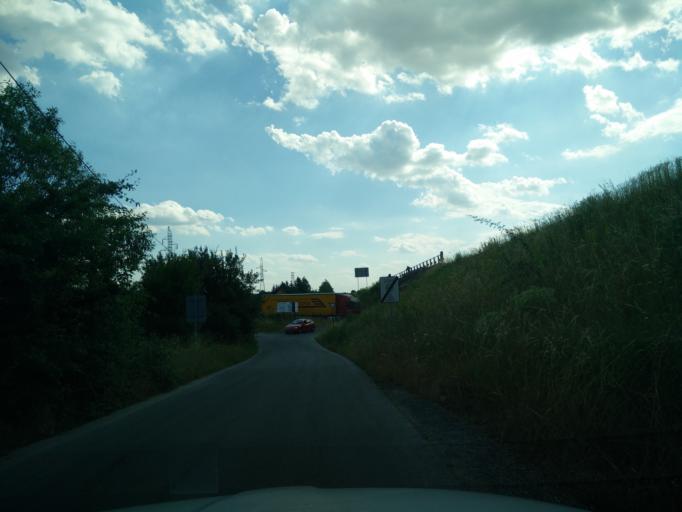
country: SK
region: Nitriansky
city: Prievidza
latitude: 48.7483
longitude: 18.6253
